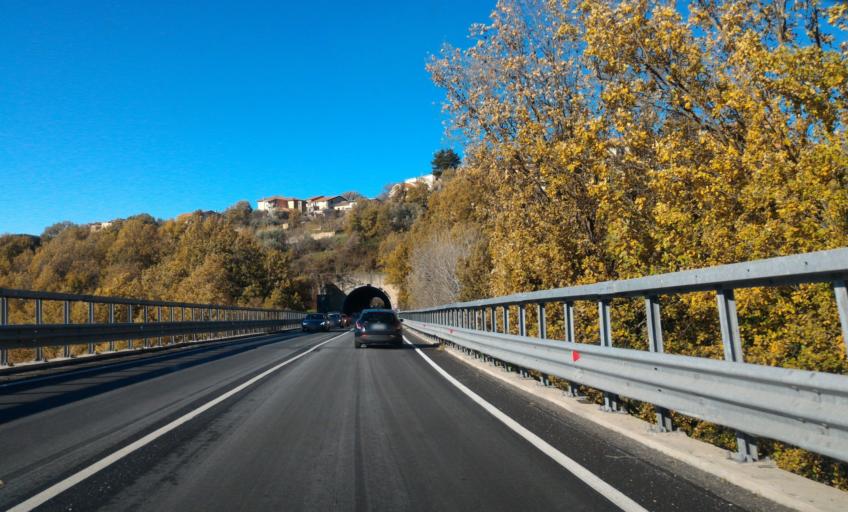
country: IT
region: Calabria
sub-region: Provincia di Cosenza
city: Rovito
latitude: 39.3048
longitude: 16.3208
